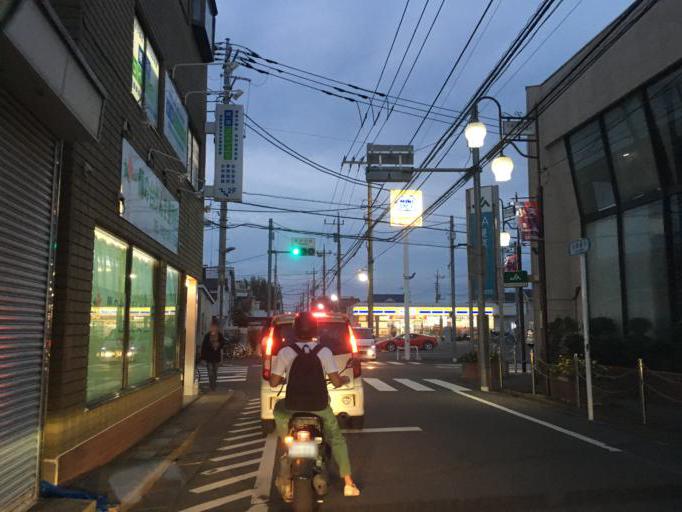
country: JP
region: Tokyo
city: Kokubunji
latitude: 35.7247
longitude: 139.4575
